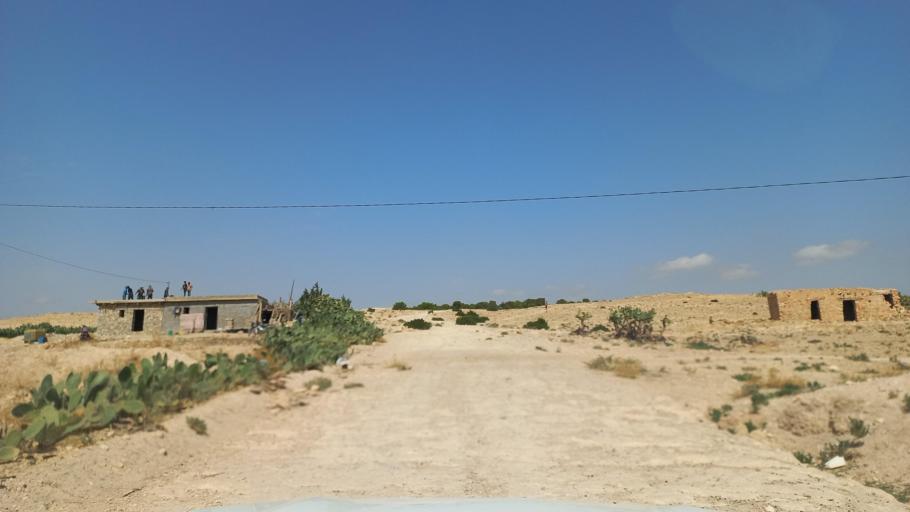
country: TN
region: Al Qasrayn
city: Sbiba
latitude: 35.4011
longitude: 8.9664
